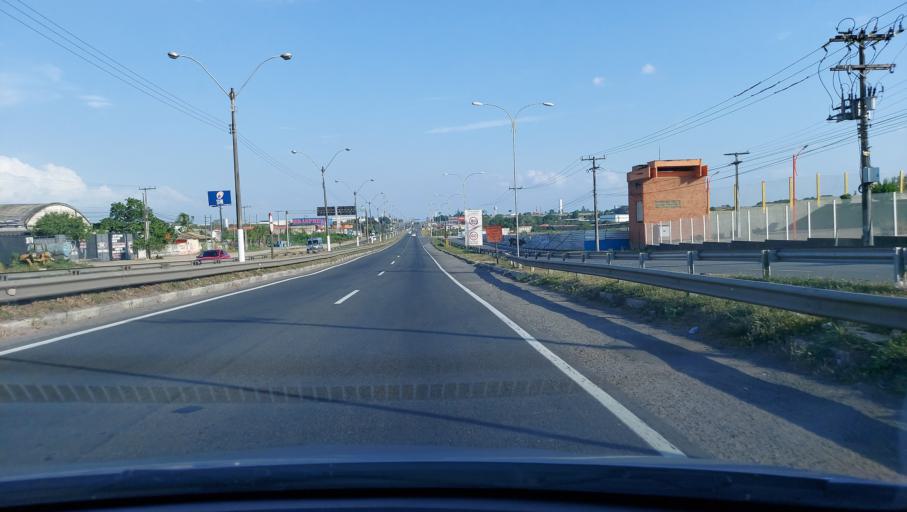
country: BR
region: Bahia
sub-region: Feira De Santana
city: Feira de Santana
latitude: -12.2742
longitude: -38.9329
